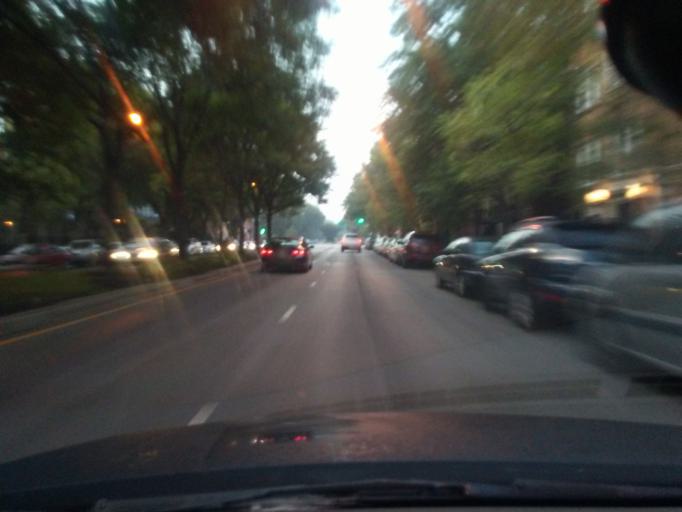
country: US
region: Illinois
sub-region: Cook County
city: Lincolnwood
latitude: 41.9626
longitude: -87.6694
